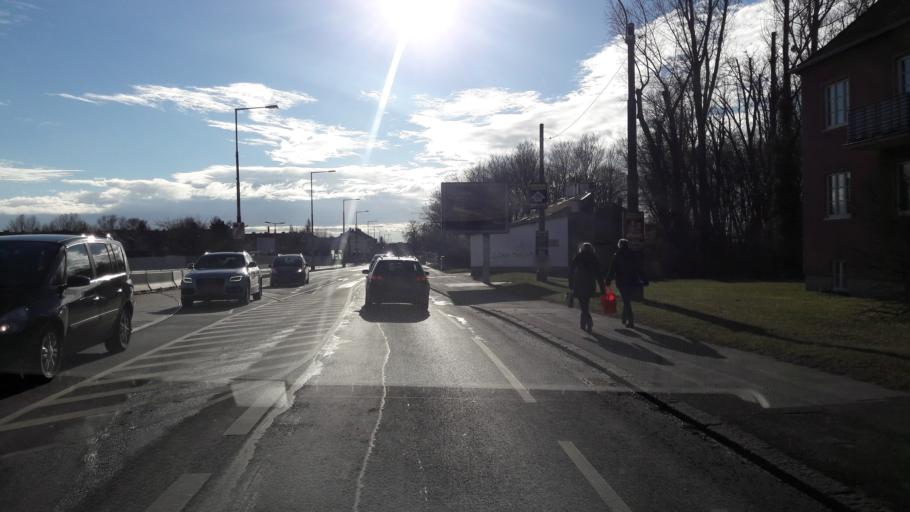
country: AT
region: Lower Austria
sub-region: Politischer Bezirk Wien-Umgebung
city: Leopoldsdorf
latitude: 48.1480
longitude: 16.3824
